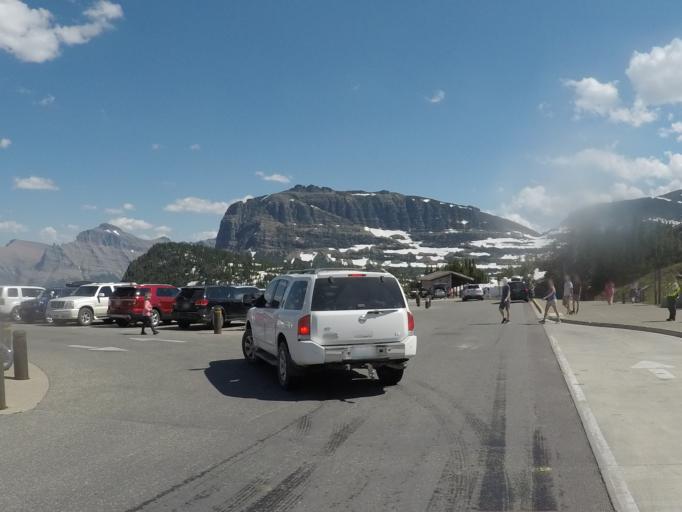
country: US
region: Montana
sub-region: Flathead County
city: Columbia Falls
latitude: 48.6961
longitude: -113.7179
